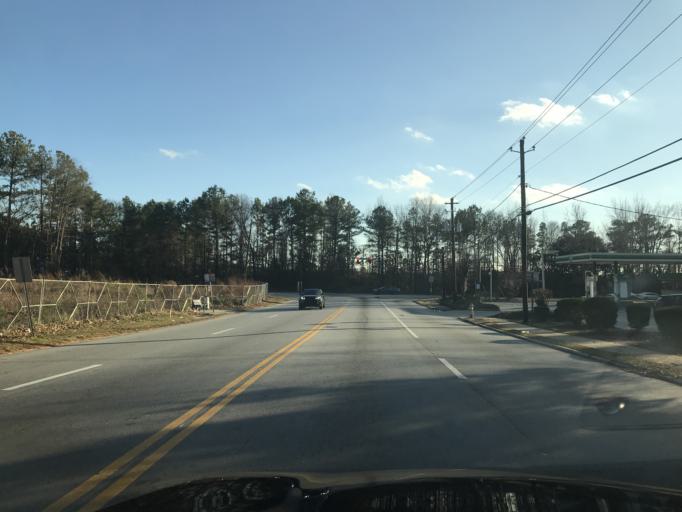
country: US
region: Georgia
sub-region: Fulton County
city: College Park
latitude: 33.6237
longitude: -84.4922
